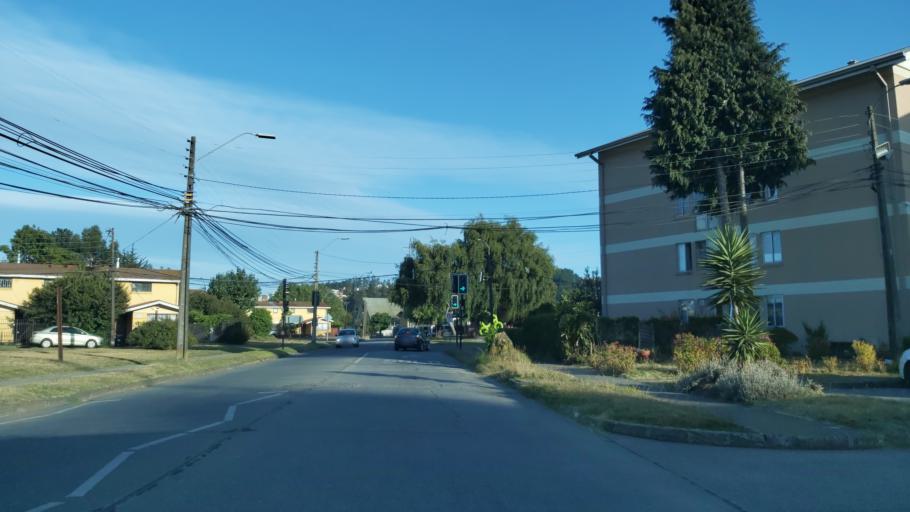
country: CL
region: Biobio
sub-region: Provincia de Concepcion
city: Concepcion
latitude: -36.8432
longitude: -73.1038
